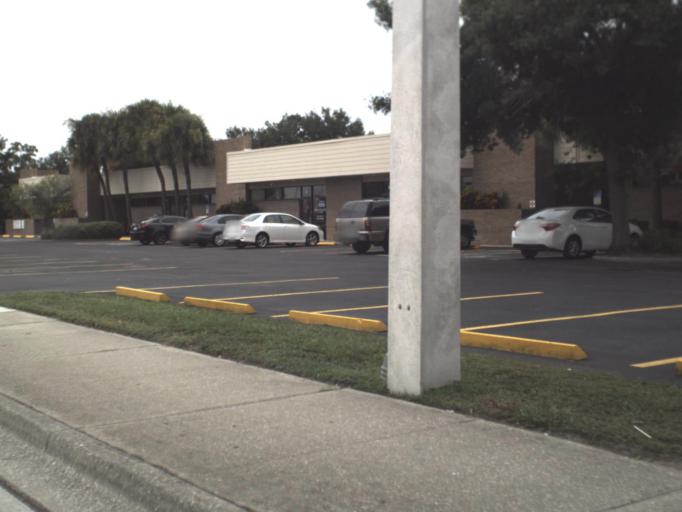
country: US
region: Florida
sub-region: Sarasota County
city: South Gate Ridge
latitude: 27.2989
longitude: -82.4924
